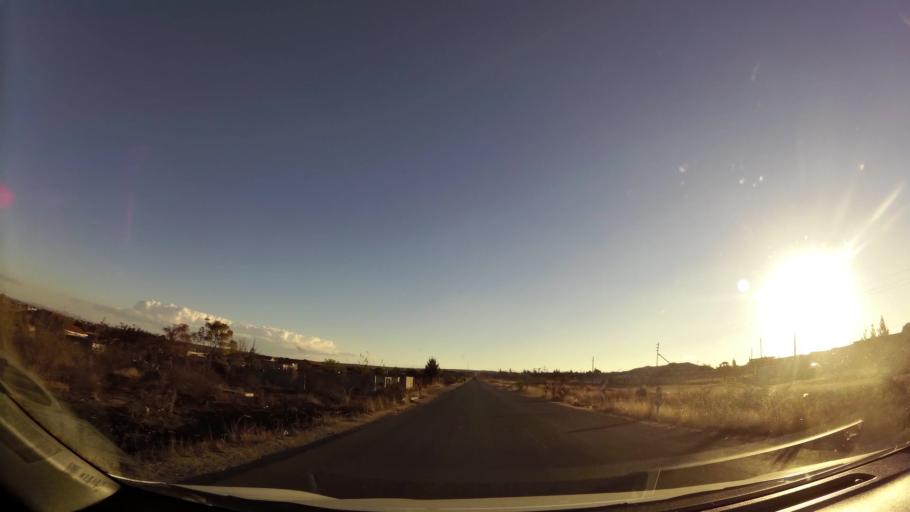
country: ZA
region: Limpopo
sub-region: Capricorn District Municipality
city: Polokwane
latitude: -23.8373
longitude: 29.3570
